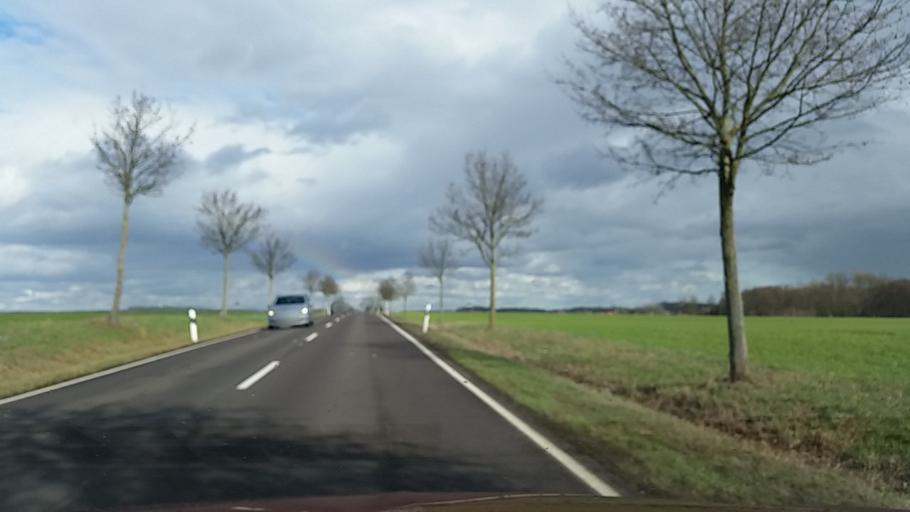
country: DE
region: Saxony-Anhalt
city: Rohrberg
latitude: 52.7423
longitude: 11.0662
